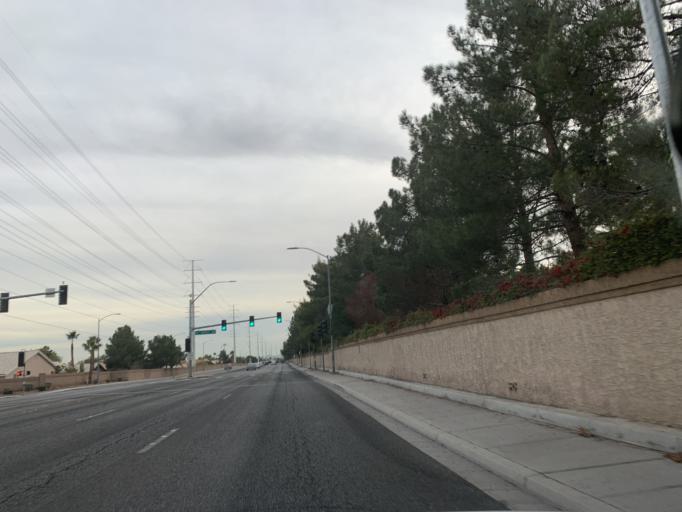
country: US
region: Nevada
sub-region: Clark County
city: Spring Valley
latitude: 36.1520
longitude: -115.2799
